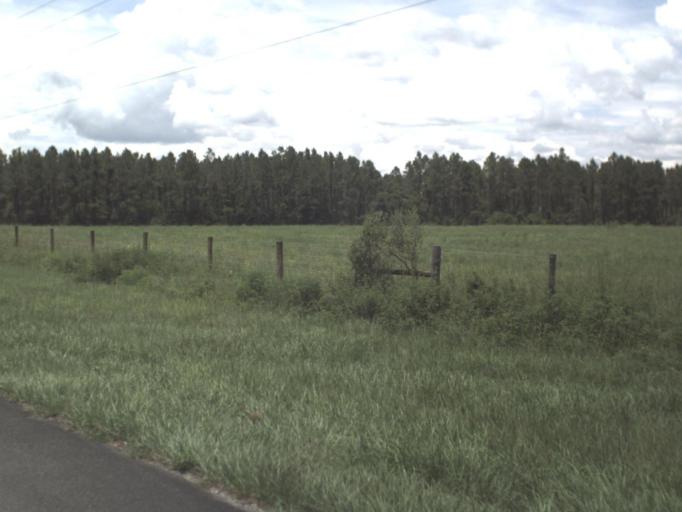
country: US
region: Florida
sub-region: Levy County
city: Williston
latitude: 29.4302
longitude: -82.4599
